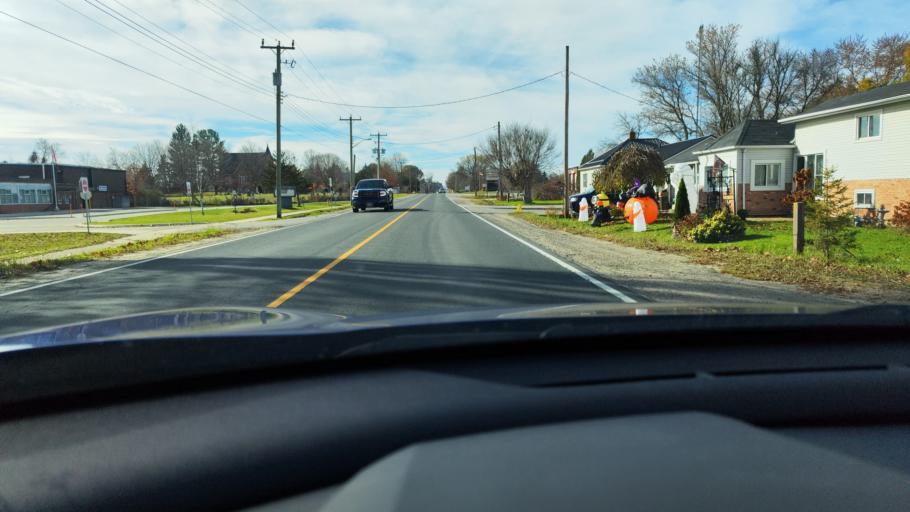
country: CA
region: Ontario
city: Angus
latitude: 44.3595
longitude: -79.9663
